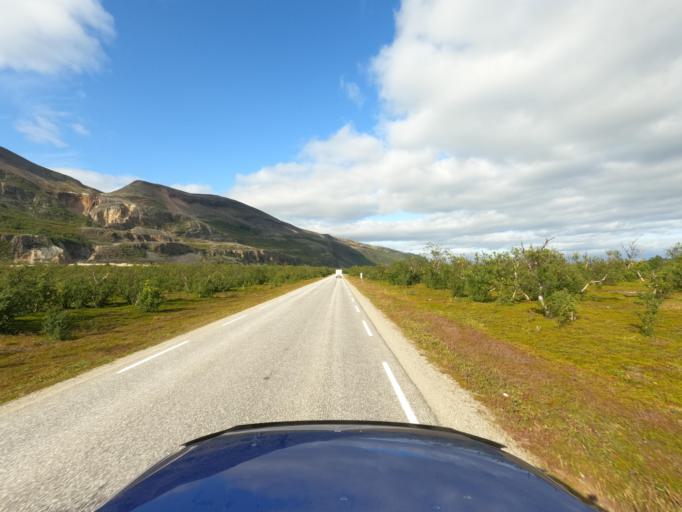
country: NO
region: Finnmark Fylke
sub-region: Porsanger
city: Lakselv
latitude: 70.0703
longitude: 24.9264
